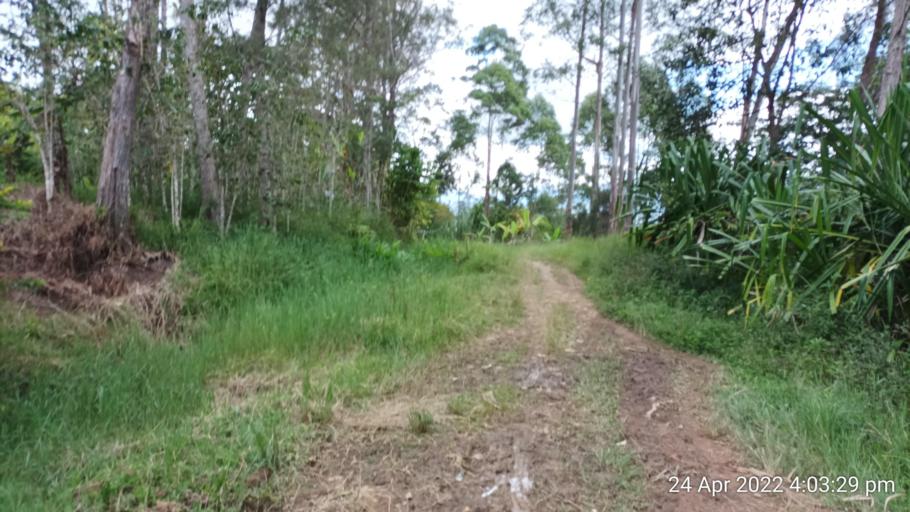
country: PG
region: Jiwaka
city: Minj
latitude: -5.9019
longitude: 144.8229
